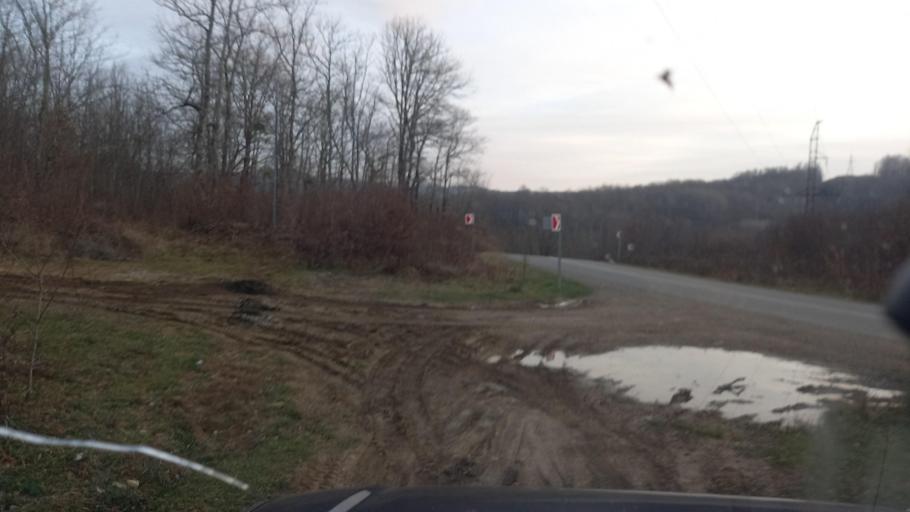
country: RU
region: Krasnodarskiy
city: Goryachiy Klyuch
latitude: 44.3873
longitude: 39.1823
